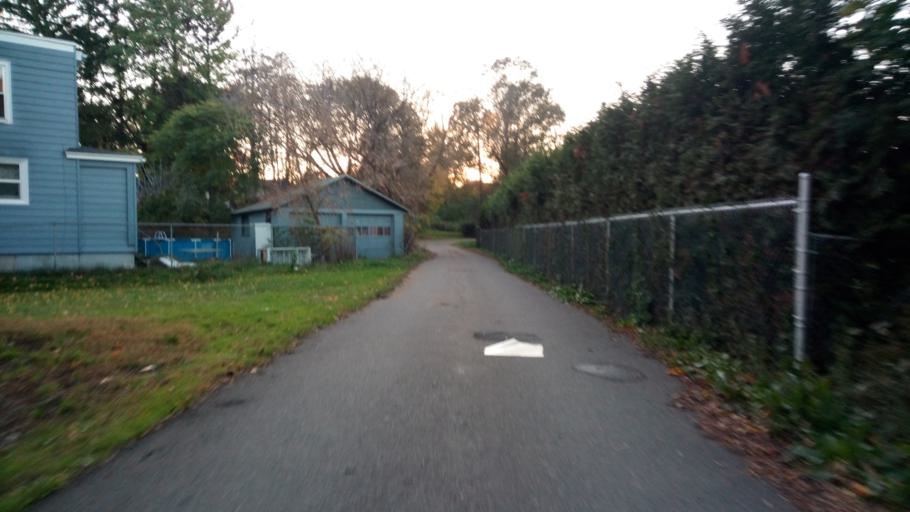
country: US
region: New York
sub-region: Chemung County
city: Elmira
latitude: 42.0803
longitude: -76.8094
